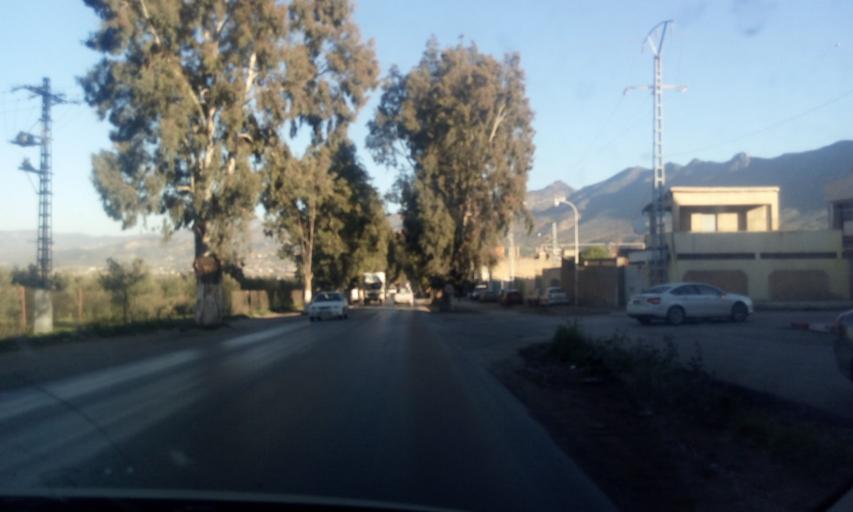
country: DZ
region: Bejaia
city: Akbou
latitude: 36.4831
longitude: 4.5628
